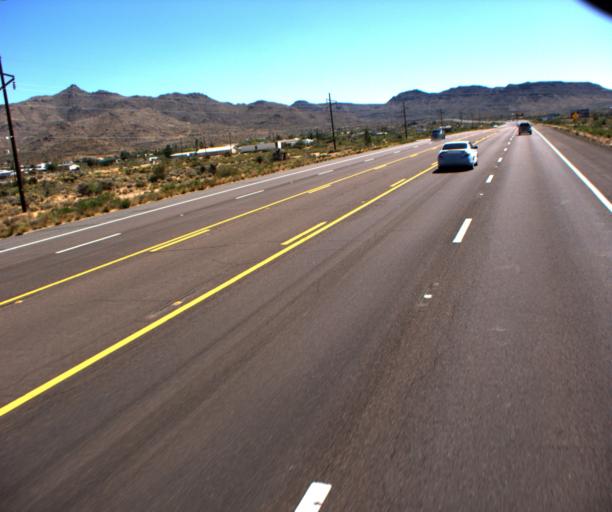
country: US
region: Arizona
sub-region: Mohave County
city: Golden Valley
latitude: 35.2188
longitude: -114.1514
